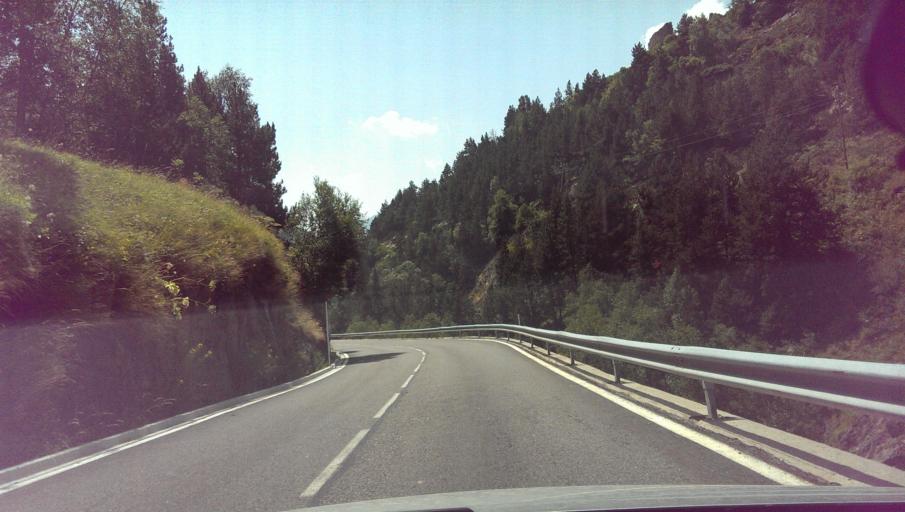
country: AD
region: Encamp
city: Pas de la Casa
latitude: 42.5453
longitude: 1.8261
